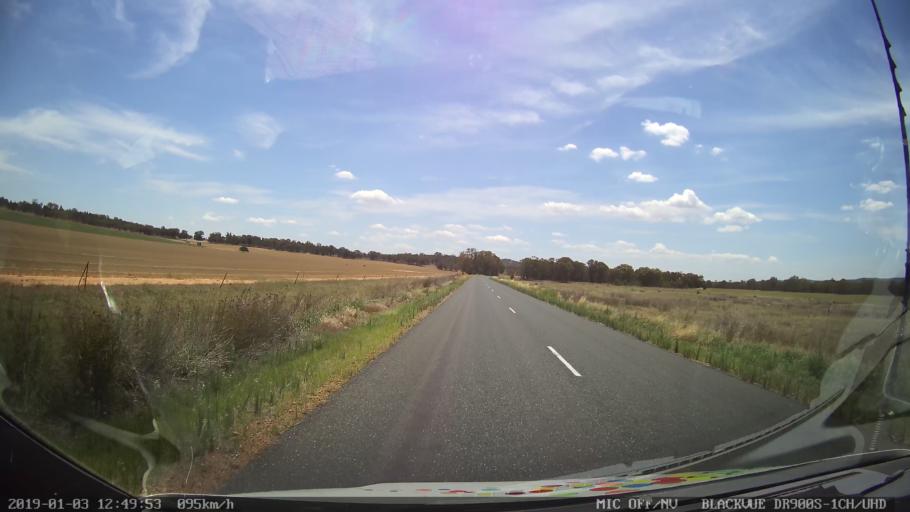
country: AU
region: New South Wales
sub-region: Weddin
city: Grenfell
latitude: -33.6977
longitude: 148.2647
